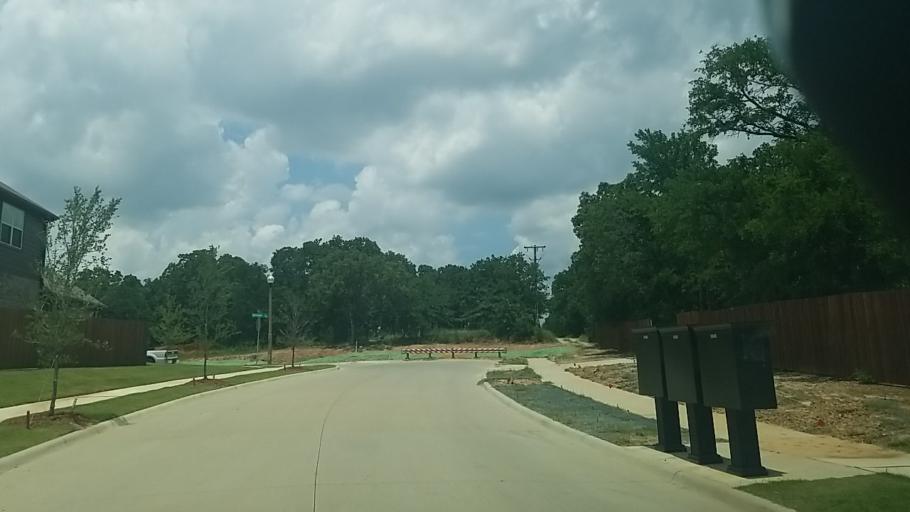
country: US
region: Texas
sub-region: Denton County
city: Corinth
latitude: 33.1682
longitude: -97.1132
